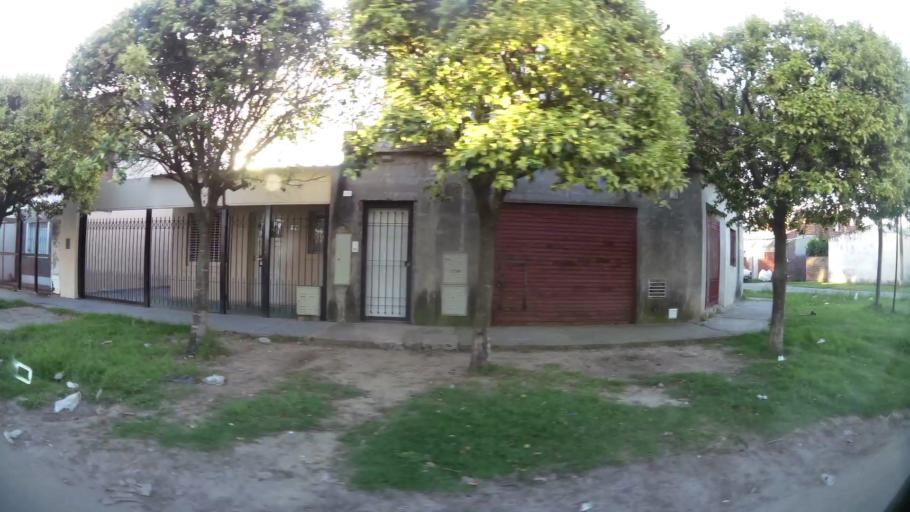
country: AR
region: Santa Fe
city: Santa Fe de la Vera Cruz
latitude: -31.5980
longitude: -60.6851
